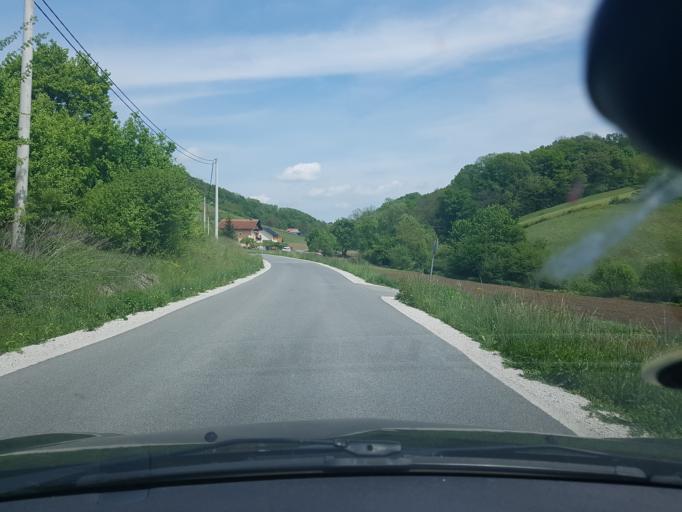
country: HR
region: Krapinsko-Zagorska
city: Pregrada
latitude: 46.1961
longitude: 15.7260
